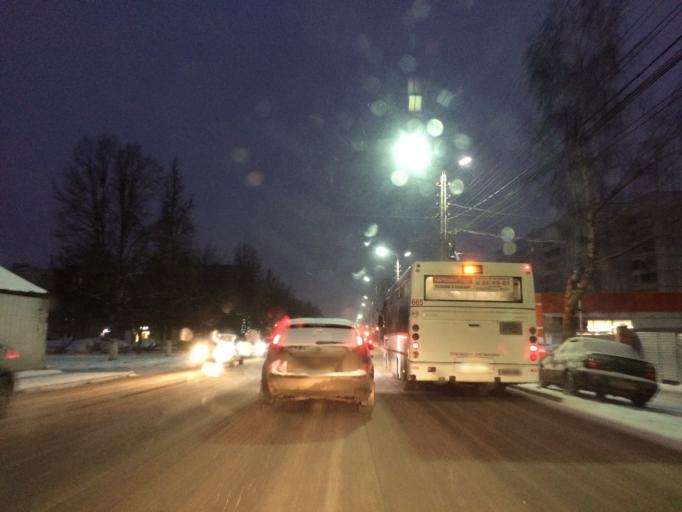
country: RU
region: Tula
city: Tula
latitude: 54.2047
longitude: 37.6528
